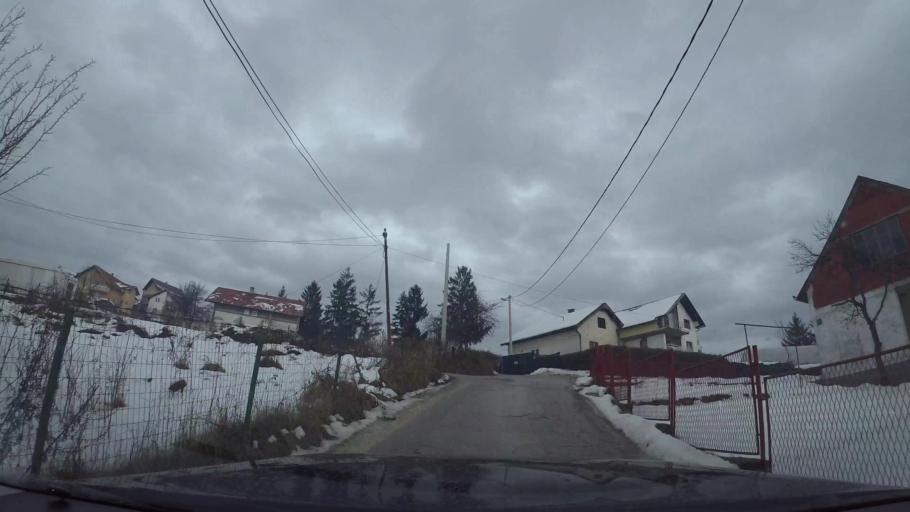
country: BA
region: Federation of Bosnia and Herzegovina
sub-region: Kanton Sarajevo
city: Sarajevo
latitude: 43.8570
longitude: 18.3339
